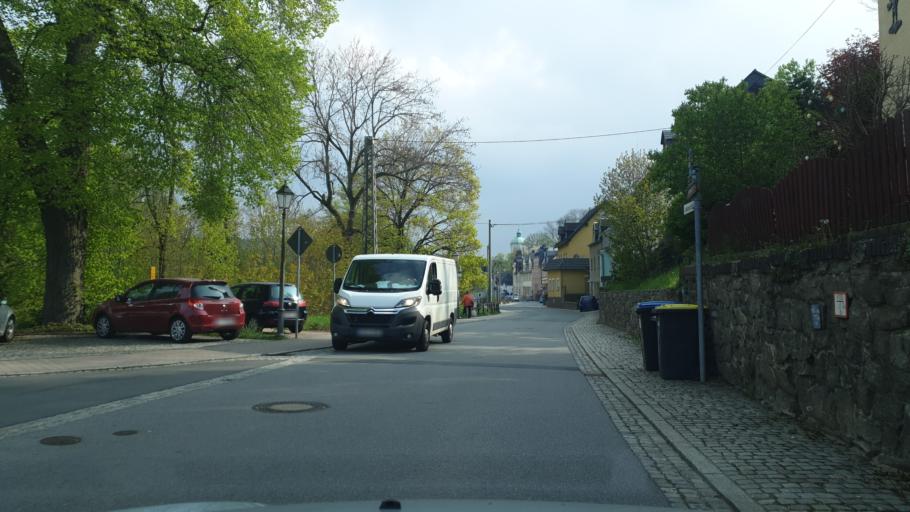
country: DE
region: Saxony
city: Lossnitz
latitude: 50.6267
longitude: 12.7351
